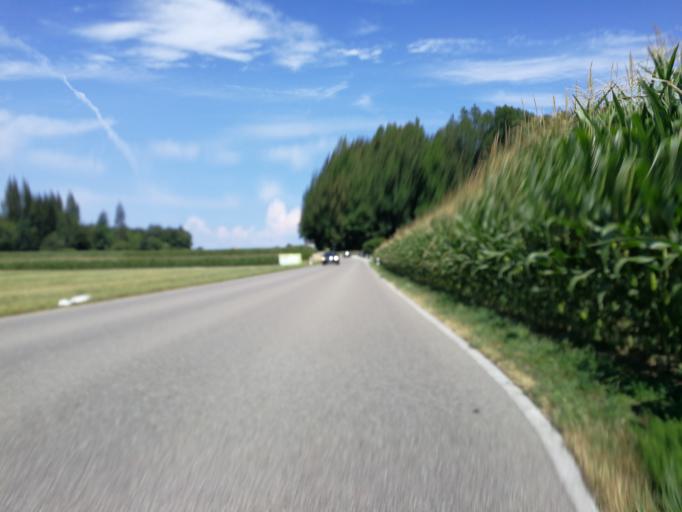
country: CH
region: Zurich
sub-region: Bezirk Hinwil
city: Wetzikon / Kempten
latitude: 47.3171
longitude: 8.8188
